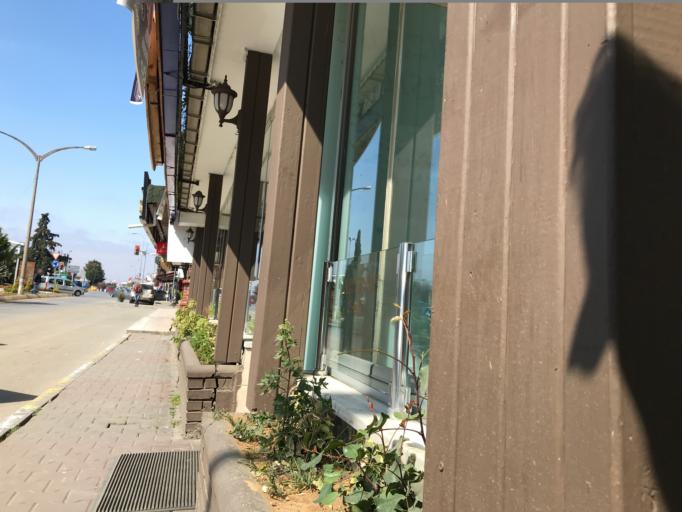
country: TR
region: Istanbul
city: Maltepe
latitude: 40.9229
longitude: 29.1272
